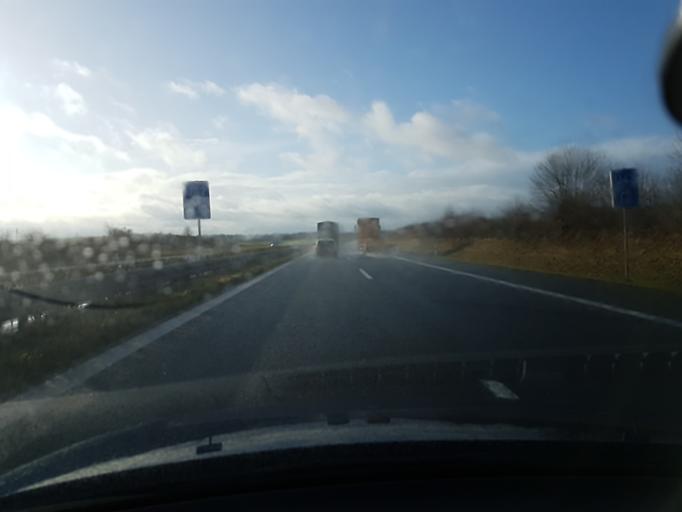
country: DE
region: Mecklenburg-Vorpommern
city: Tessin
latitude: 54.0160
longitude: 12.5558
